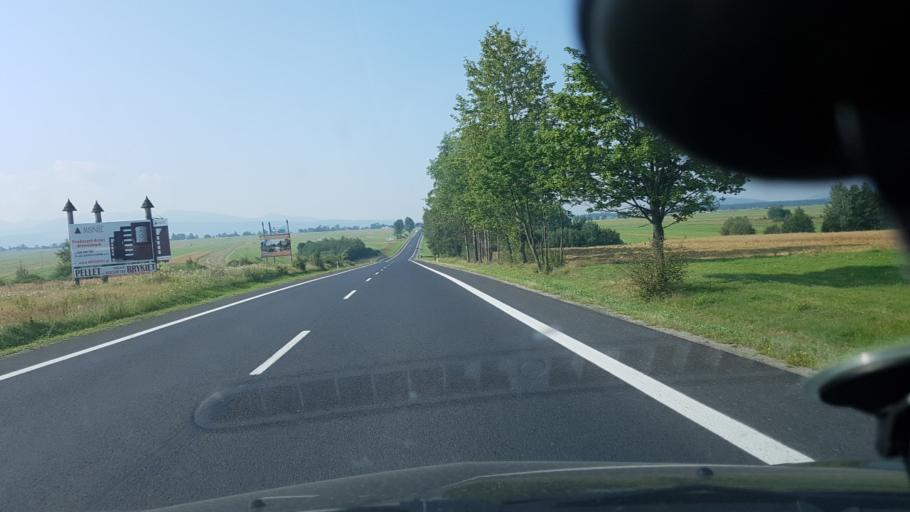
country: PL
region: Lesser Poland Voivodeship
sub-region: Powiat nowotarski
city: Chyzne
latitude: 49.4434
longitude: 19.6834
